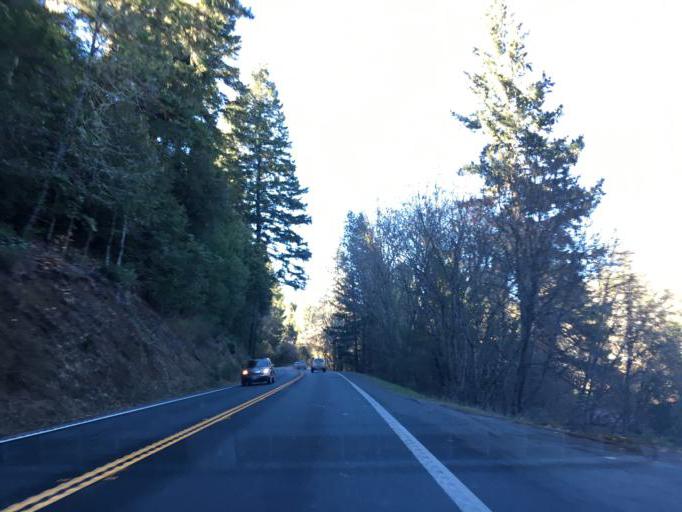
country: US
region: California
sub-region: Mendocino County
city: Brooktrails
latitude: 39.4877
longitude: -123.3615
